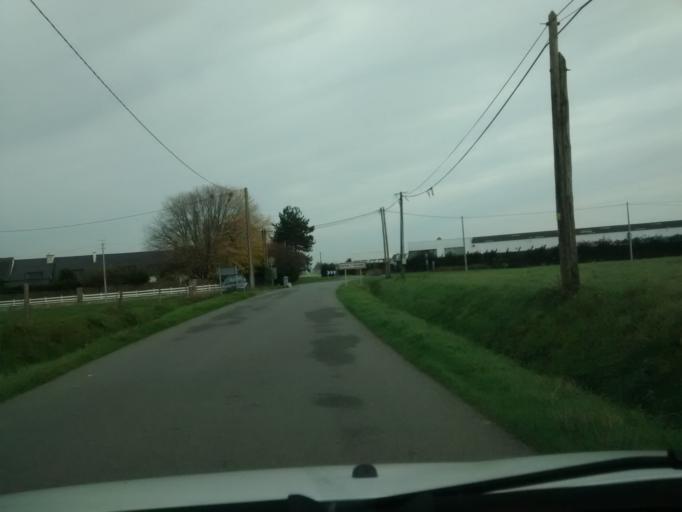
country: FR
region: Brittany
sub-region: Departement d'Ille-et-Vilaine
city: Noyal-sur-Vilaine
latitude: 48.1071
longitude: -1.5333
